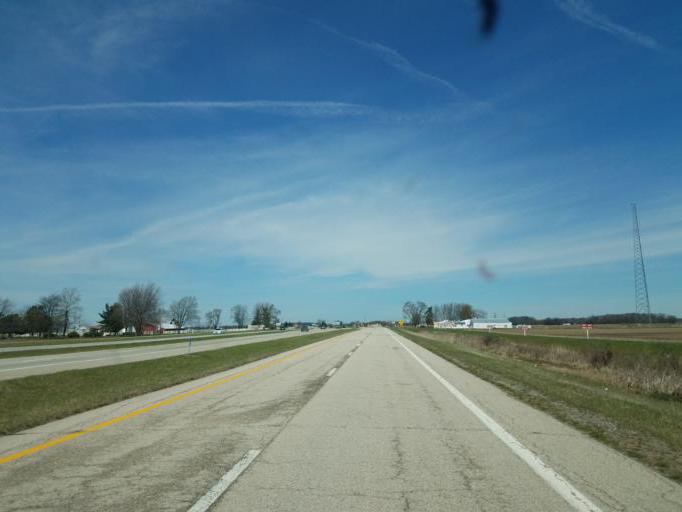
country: US
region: Ohio
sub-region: Delaware County
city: Delaware
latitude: 40.4099
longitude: -83.0738
